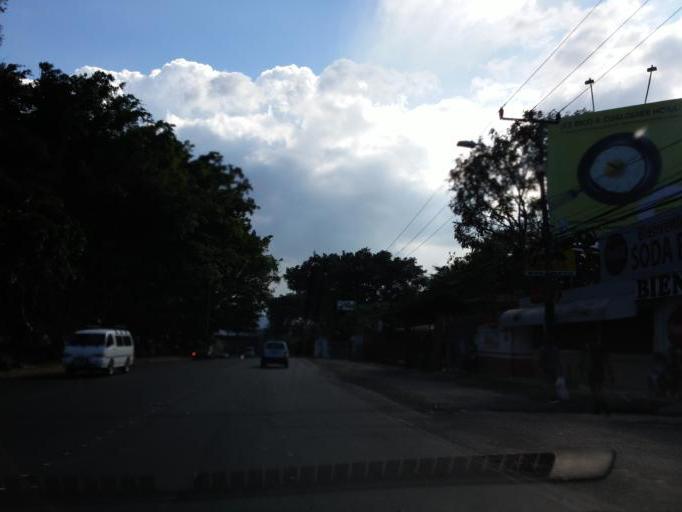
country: CR
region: Heredia
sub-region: Canton de Belen
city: San Antonio
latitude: 9.9780
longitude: -84.1993
